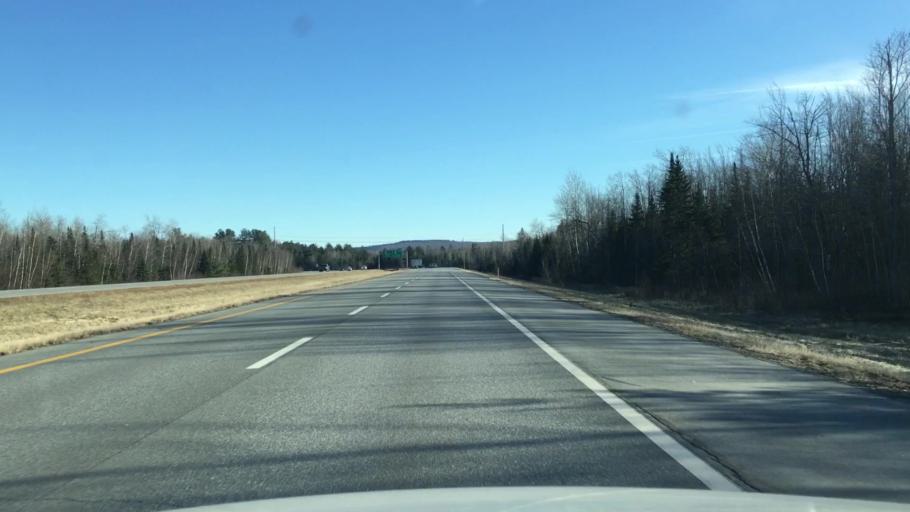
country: US
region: Maine
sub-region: Penobscot County
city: Brewer
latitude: 44.7704
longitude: -68.7396
